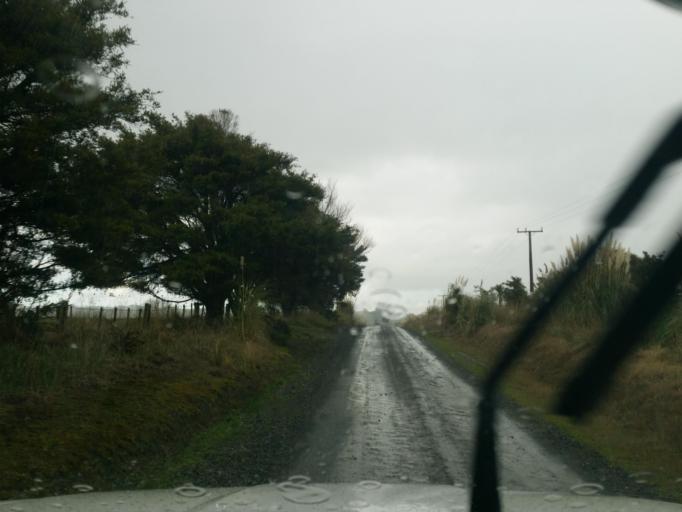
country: NZ
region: Northland
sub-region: Whangarei
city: Maungatapere
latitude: -36.0512
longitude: 174.1761
